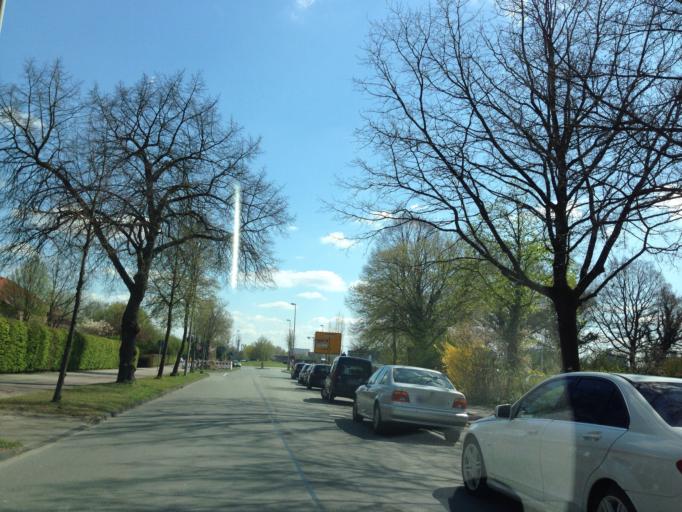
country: DE
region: North Rhine-Westphalia
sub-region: Regierungsbezirk Munster
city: Muenster
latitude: 51.9746
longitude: 7.5884
